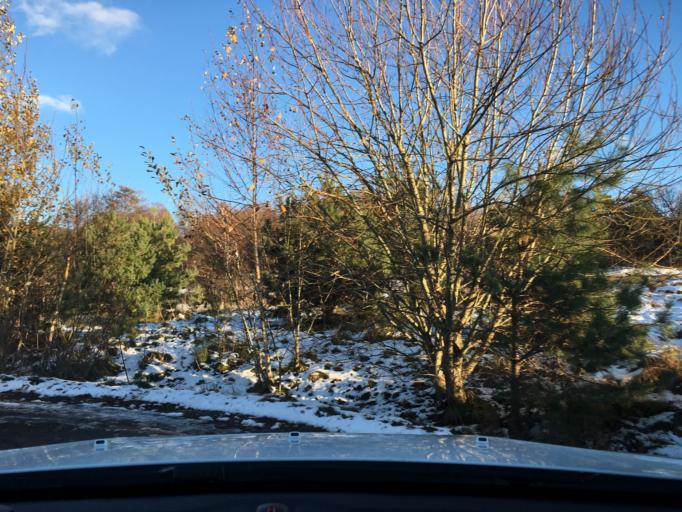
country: SE
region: Vaestra Goetaland
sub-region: Stenungsunds Kommun
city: Stenungsund
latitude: 58.0514
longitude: 11.8173
